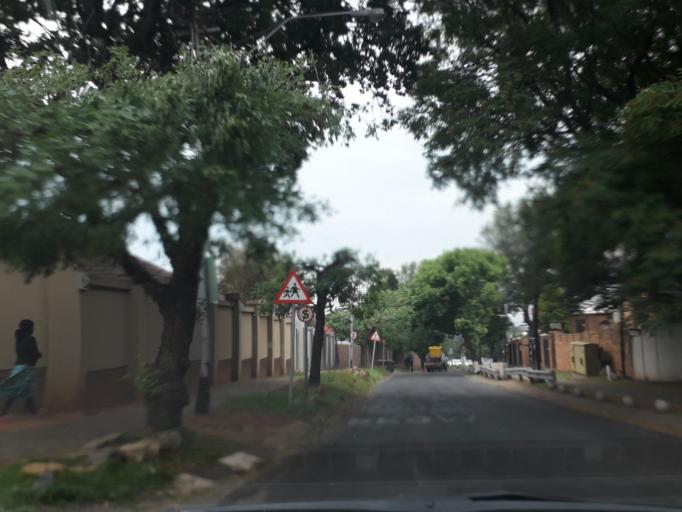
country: ZA
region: Gauteng
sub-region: City of Johannesburg Metropolitan Municipality
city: Johannesburg
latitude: -26.1395
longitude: 28.0970
